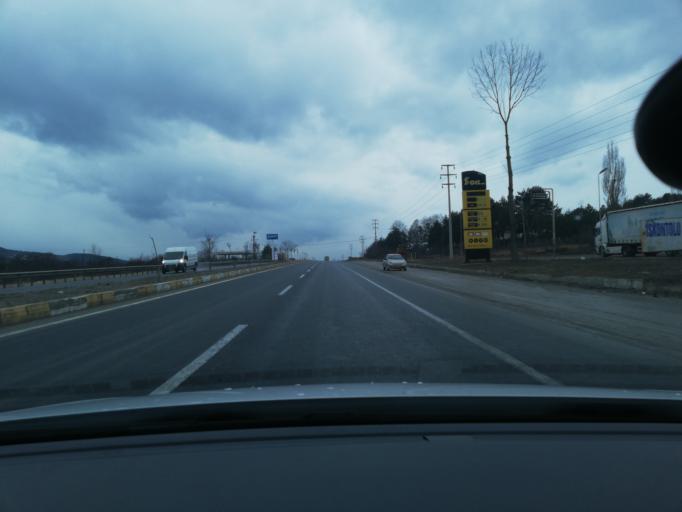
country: TR
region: Bolu
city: Yenicaga
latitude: 40.7579
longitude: 31.9247
